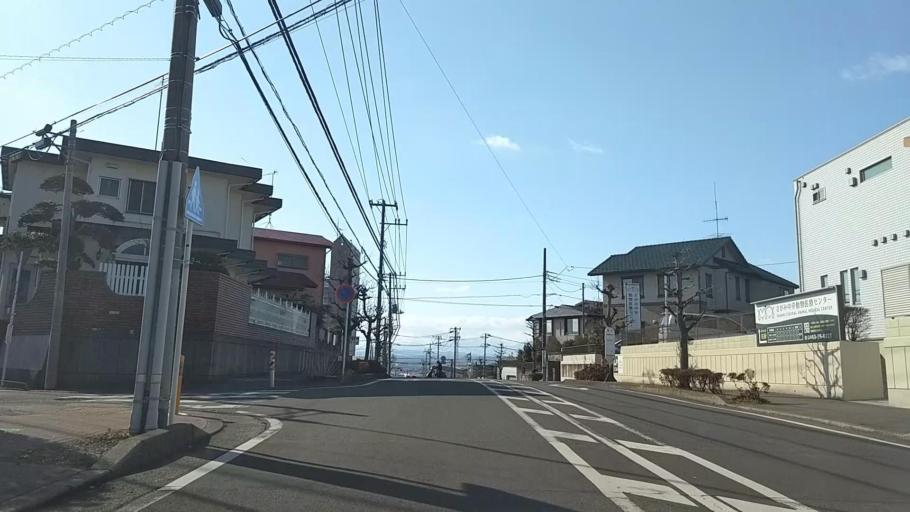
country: JP
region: Kanagawa
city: Isehara
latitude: 35.3942
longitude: 139.3043
